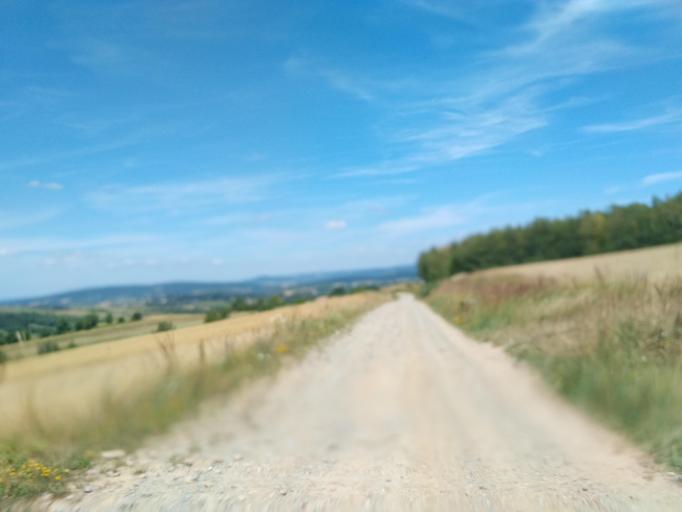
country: PL
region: Subcarpathian Voivodeship
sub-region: Powiat sanocki
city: Bukowsko
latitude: 49.5009
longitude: 22.0957
